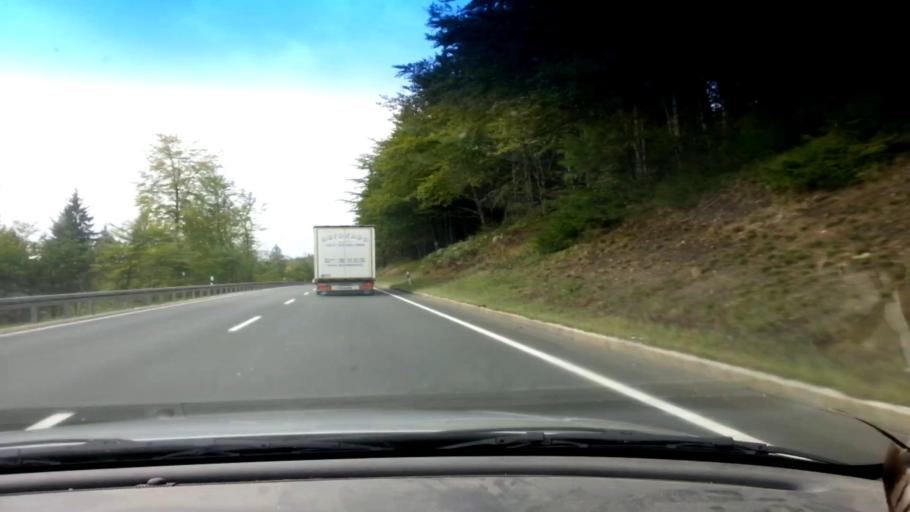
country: DE
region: Bavaria
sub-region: Upper Franconia
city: Fichtelberg
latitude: 50.0076
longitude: 11.8881
